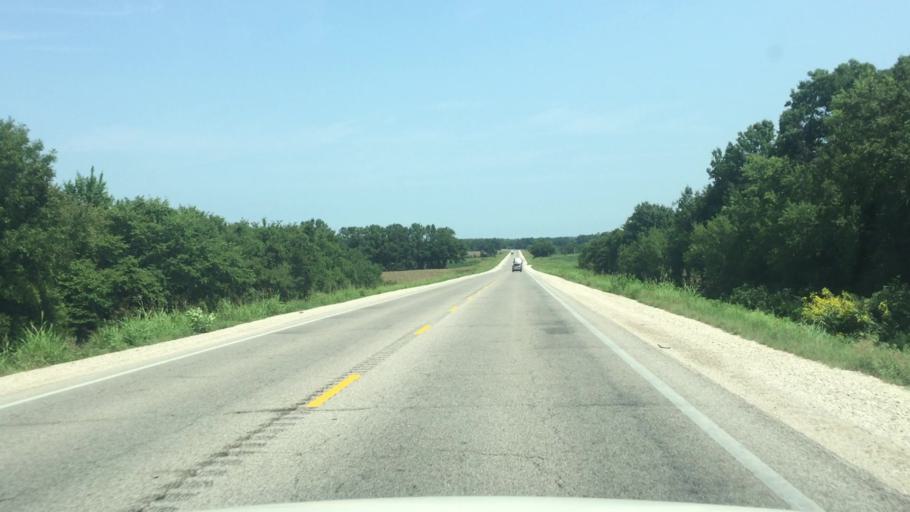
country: US
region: Kansas
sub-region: Montgomery County
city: Cherryvale
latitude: 37.1619
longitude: -95.5767
